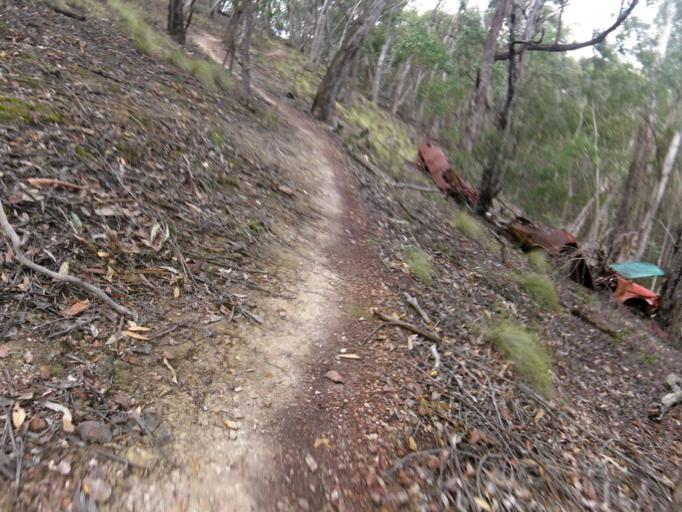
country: AU
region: Victoria
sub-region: Melton
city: Melton West
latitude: -37.4870
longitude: 144.5364
